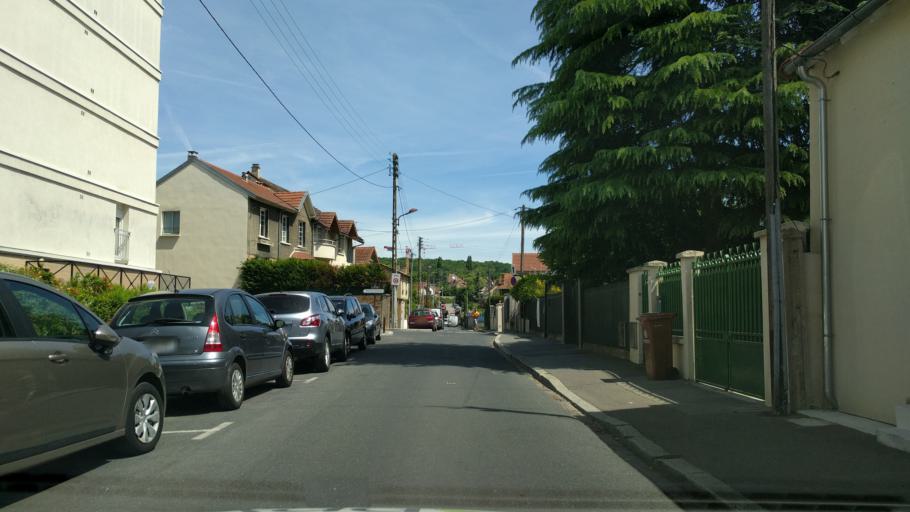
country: FR
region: Ile-de-France
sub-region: Departement des Yvelines
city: Viroflay
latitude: 48.8027
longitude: 2.1625
